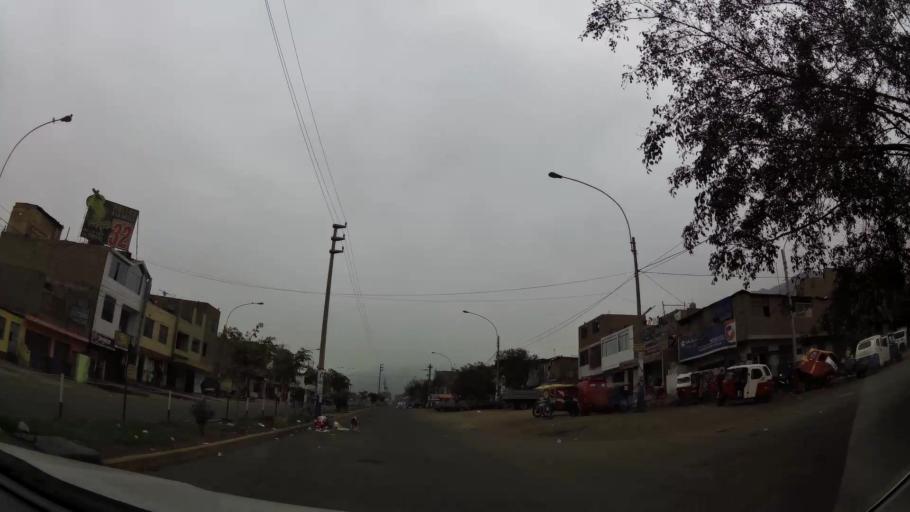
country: PE
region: Lima
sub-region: Lima
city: Independencia
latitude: -11.9661
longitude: -77.0098
